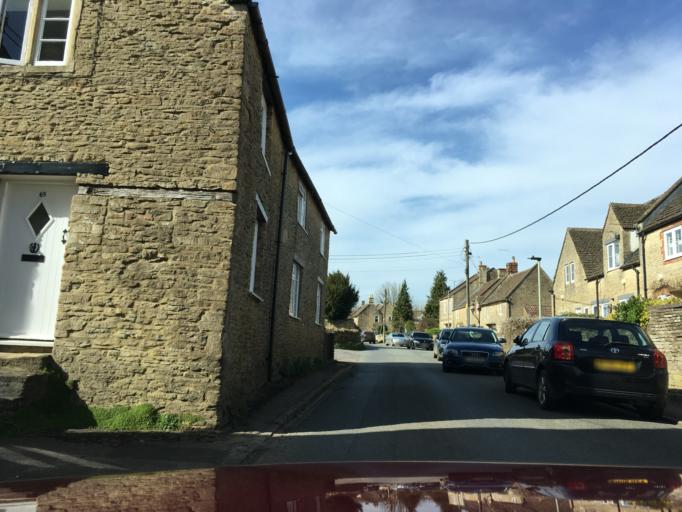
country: GB
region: England
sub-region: Wiltshire
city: Chippenham
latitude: 51.4954
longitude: -2.1398
